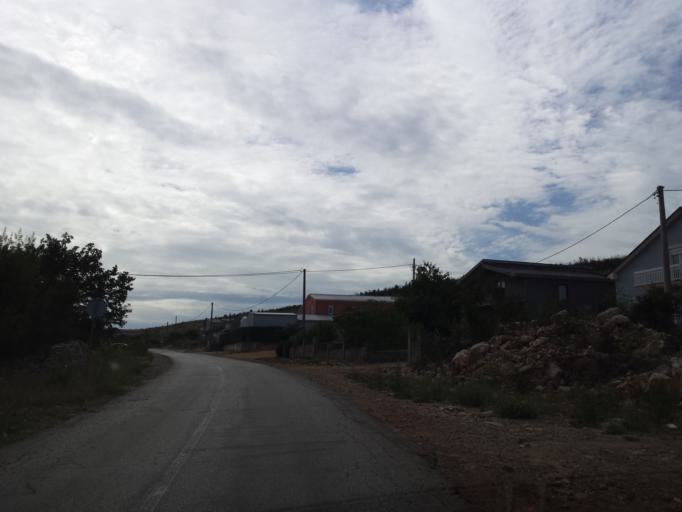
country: BA
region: Federation of Bosnia and Herzegovina
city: Capljina
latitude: 43.1673
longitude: 17.6531
